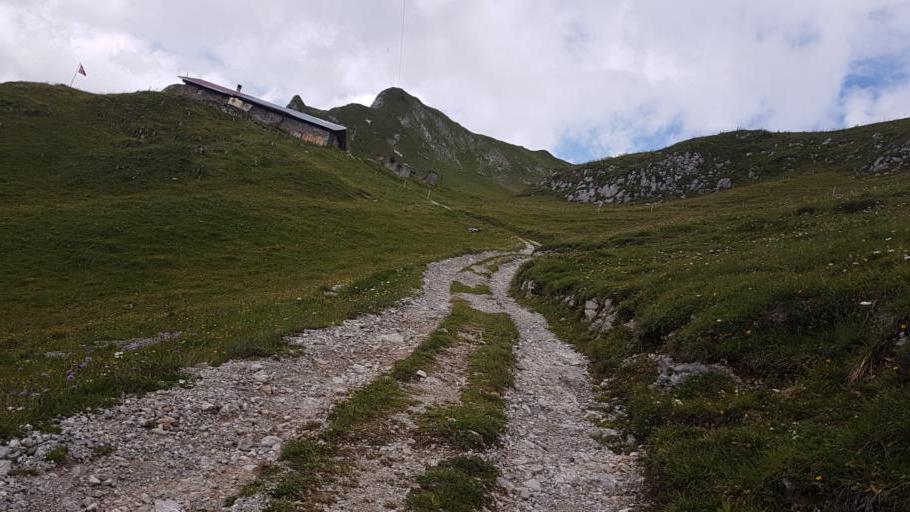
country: CH
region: Bern
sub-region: Obersimmental-Saanen District
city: Boltigen
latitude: 46.6966
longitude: 7.4433
